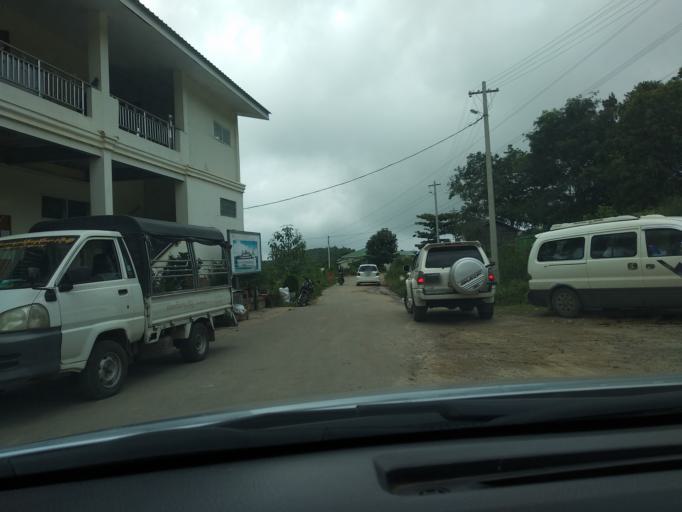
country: MM
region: Mandalay
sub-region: Pyin Oo Lwin District
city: Pyin Oo Lwin
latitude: 21.9116
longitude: 96.3841
